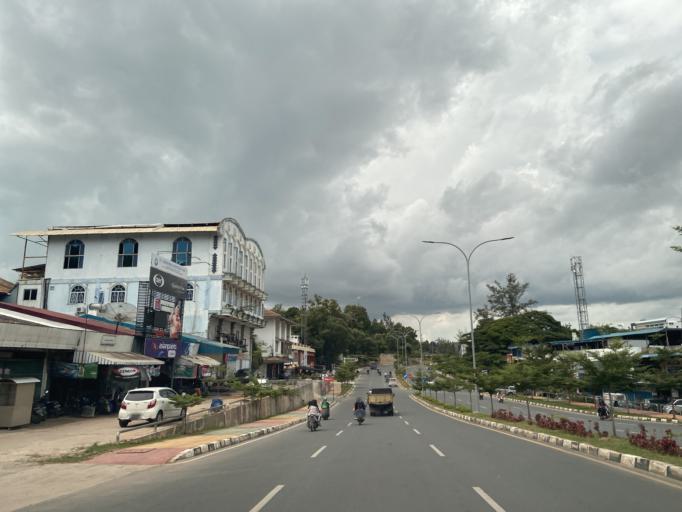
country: SG
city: Singapore
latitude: 1.1524
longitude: 104.0099
